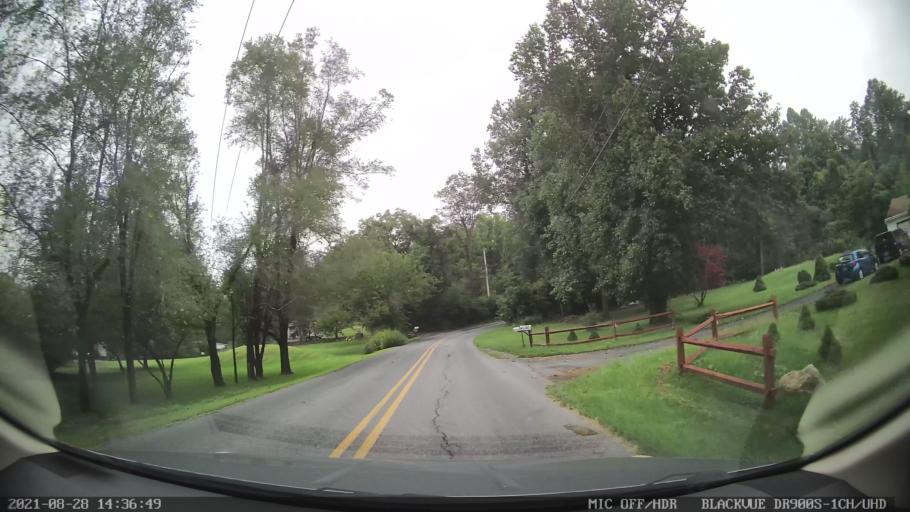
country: US
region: Pennsylvania
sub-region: Berks County
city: South Temple
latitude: 40.3858
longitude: -75.8706
